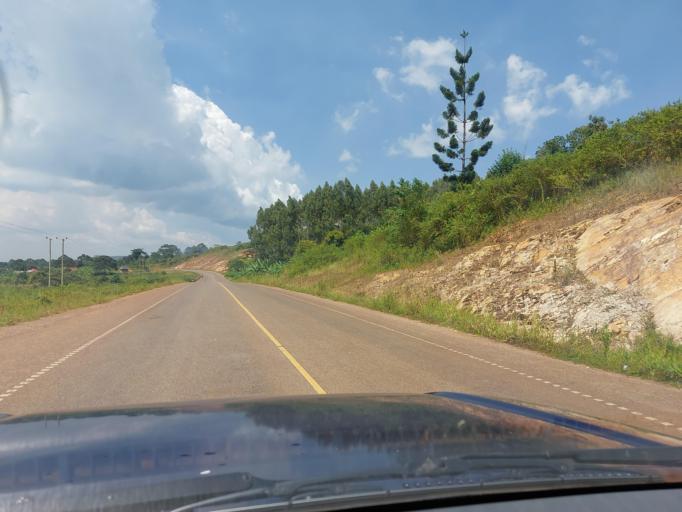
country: UG
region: Central Region
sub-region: Buikwe District
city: Buikwe
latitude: 0.2949
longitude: 33.0935
